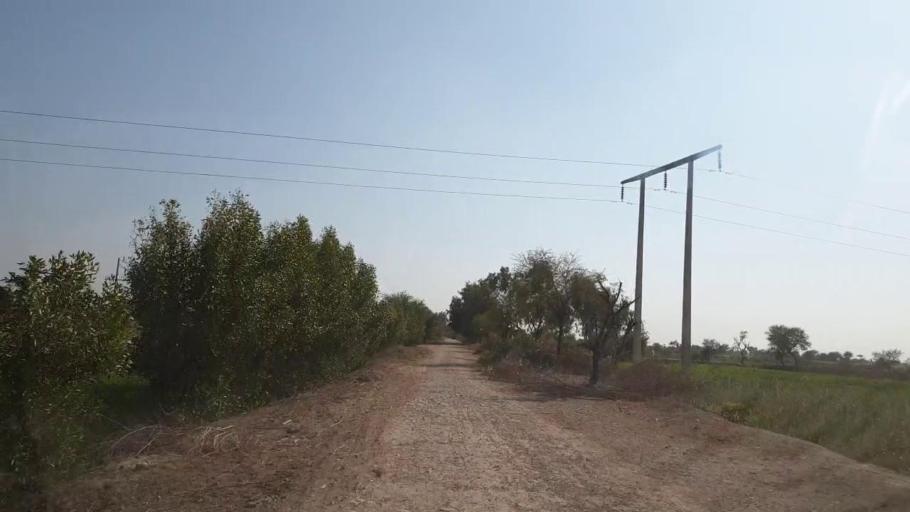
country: PK
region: Sindh
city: Mirpur Khas
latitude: 25.7211
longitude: 69.1613
